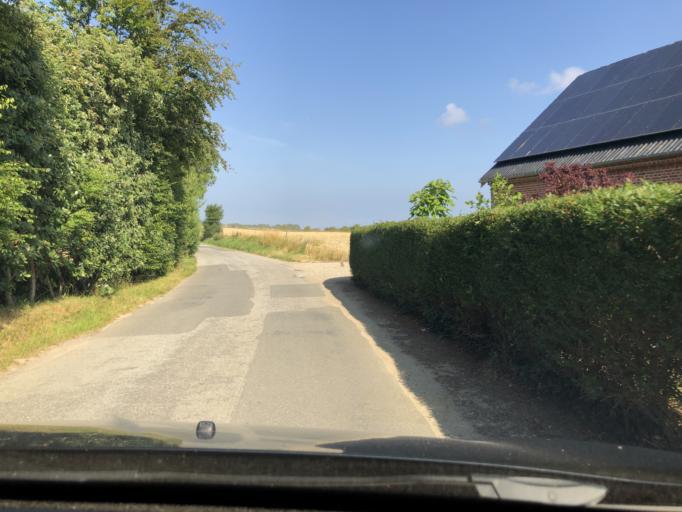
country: DK
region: South Denmark
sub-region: Faaborg-Midtfyn Kommune
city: Faaborg
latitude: 54.9428
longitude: 10.2483
